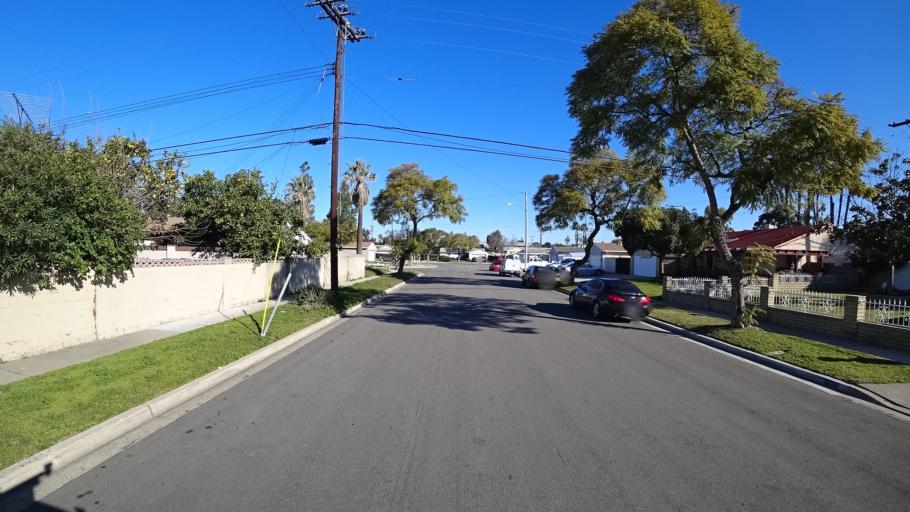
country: US
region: California
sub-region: Orange County
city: Cypress
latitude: 33.8155
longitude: -118.0135
